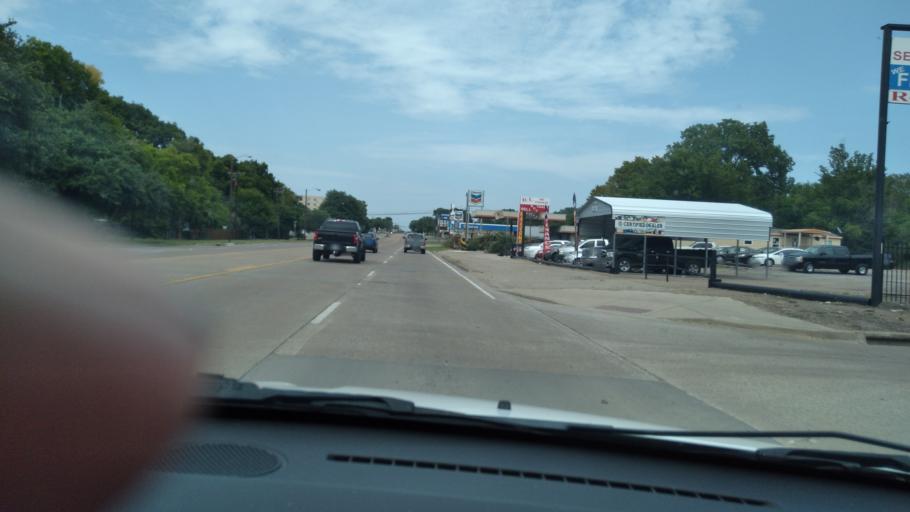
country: US
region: Texas
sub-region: Navarro County
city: Corsicana
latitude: 32.0773
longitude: -96.4932
